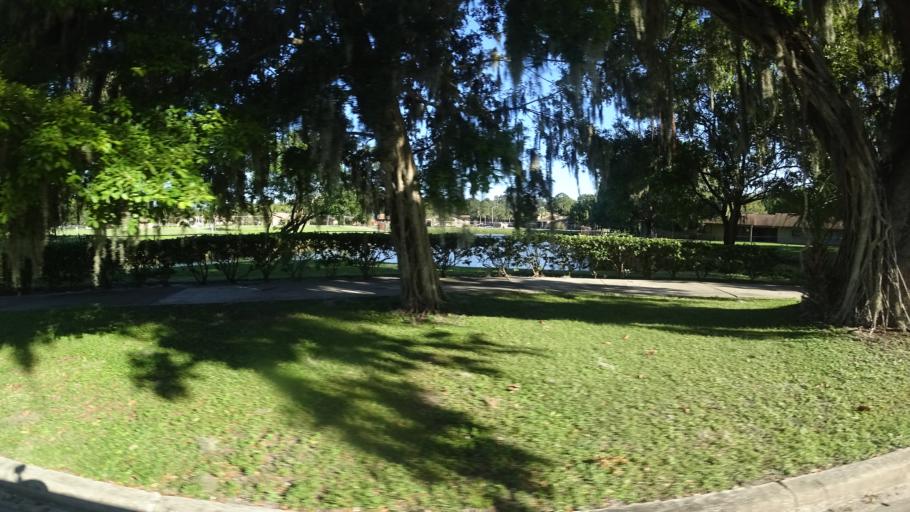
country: US
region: Florida
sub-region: Manatee County
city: Samoset
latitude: 27.4881
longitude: -82.5452
